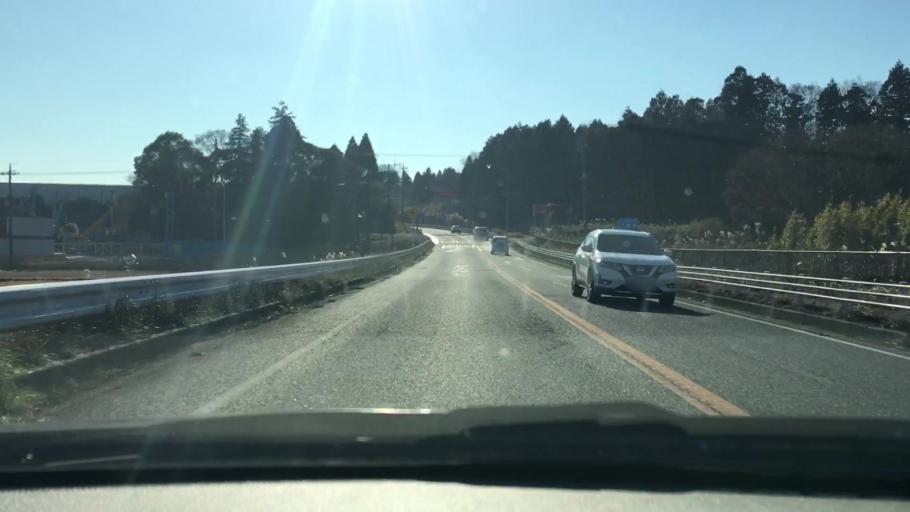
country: JP
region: Chiba
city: Sakura
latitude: 35.6946
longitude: 140.2466
